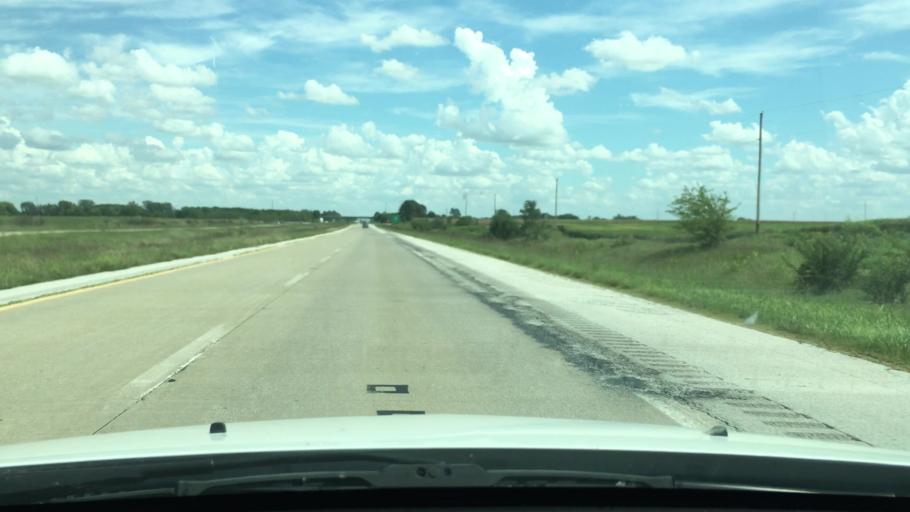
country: US
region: Illinois
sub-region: Scott County
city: Winchester
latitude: 39.6807
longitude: -90.4698
